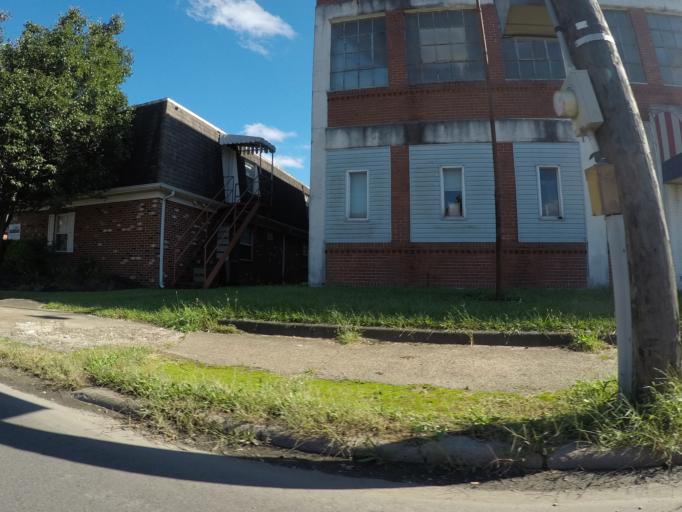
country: US
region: Ohio
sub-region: Lawrence County
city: Burlington
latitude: 38.4081
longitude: -82.4938
